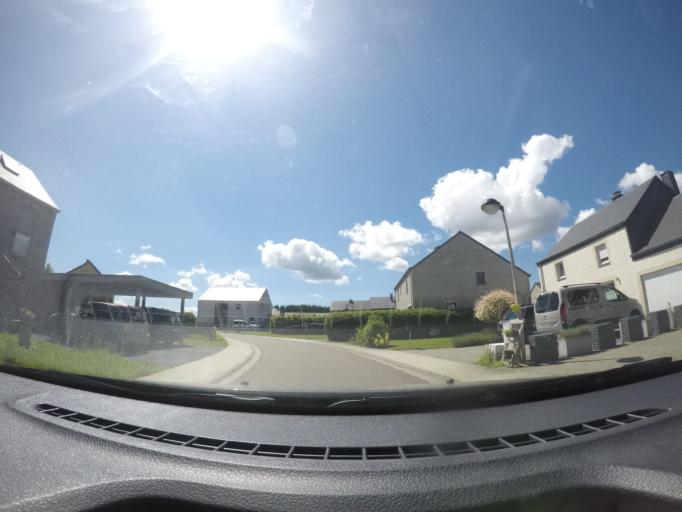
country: BE
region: Wallonia
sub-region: Province du Luxembourg
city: Tintigny
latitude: 49.6815
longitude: 5.5207
